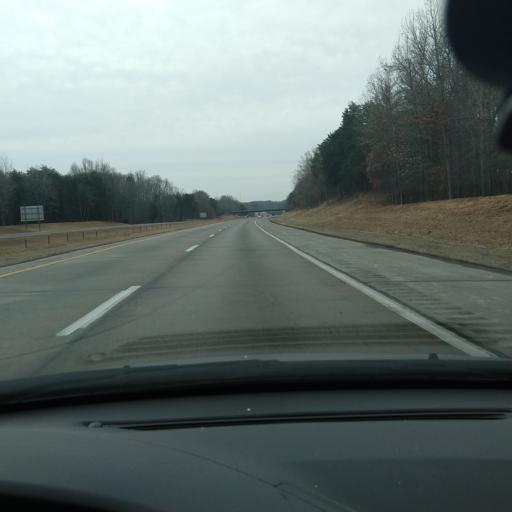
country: US
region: North Carolina
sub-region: Davidson County
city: Midway
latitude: 35.9627
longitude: -80.2306
